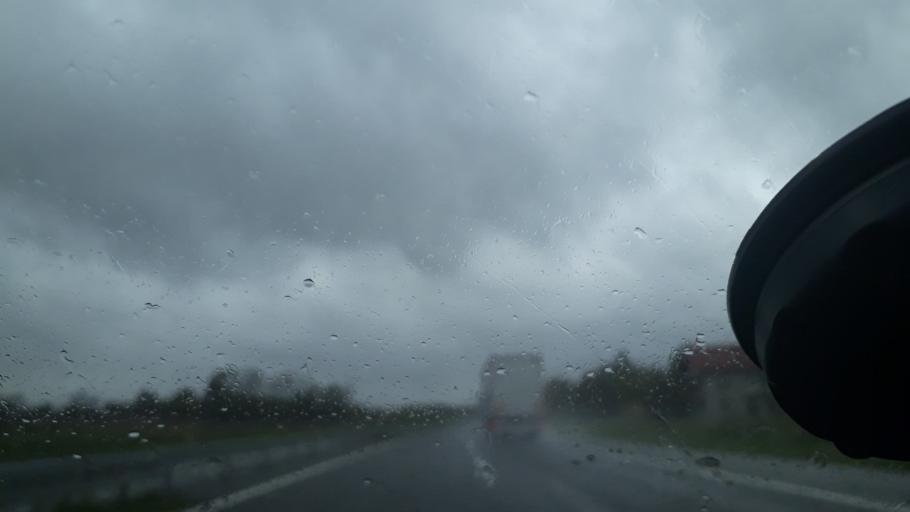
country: BA
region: Republika Srpska
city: Laktasi
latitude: 45.0066
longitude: 17.2312
